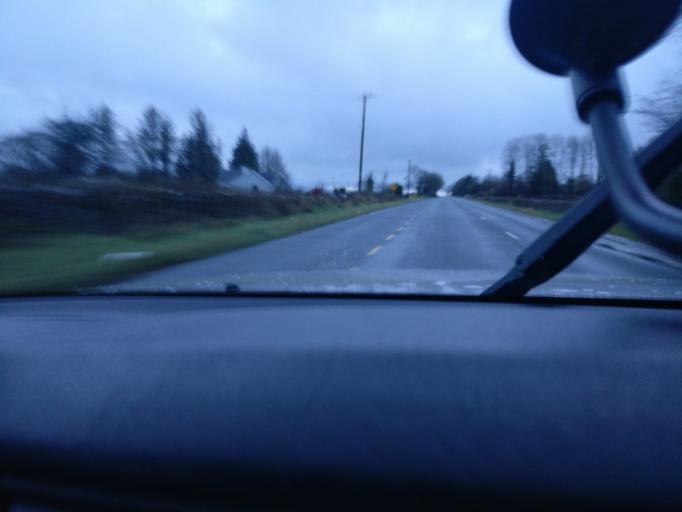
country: IE
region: Connaught
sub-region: County Galway
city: Loughrea
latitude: 53.2664
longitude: -8.4152
